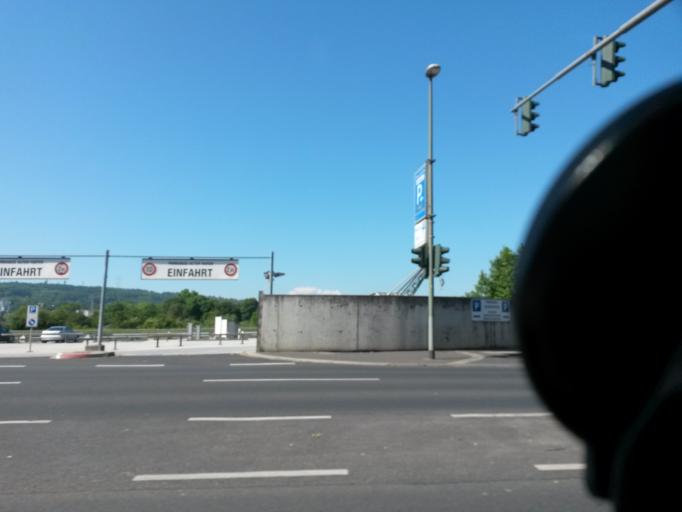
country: DE
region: Bavaria
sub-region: Regierungsbezirk Unterfranken
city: Wuerzburg
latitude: 49.8036
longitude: 9.9198
